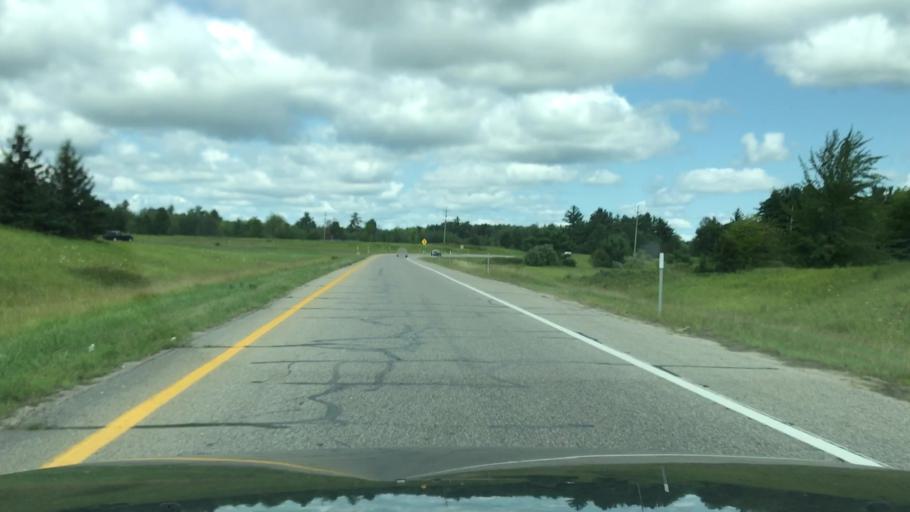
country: US
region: Michigan
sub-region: Mecosta County
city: Big Rapids
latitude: 43.6893
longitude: -85.5196
